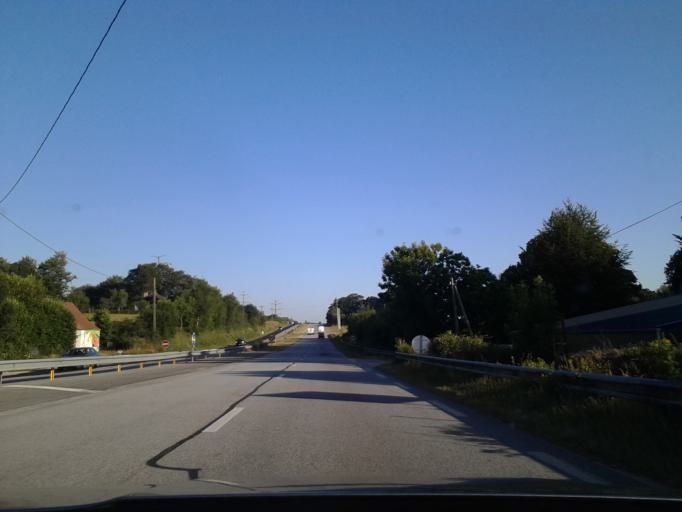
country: FR
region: Lower Normandy
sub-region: Departement de la Manche
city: La Glacerie
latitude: 49.5792
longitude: -1.5842
